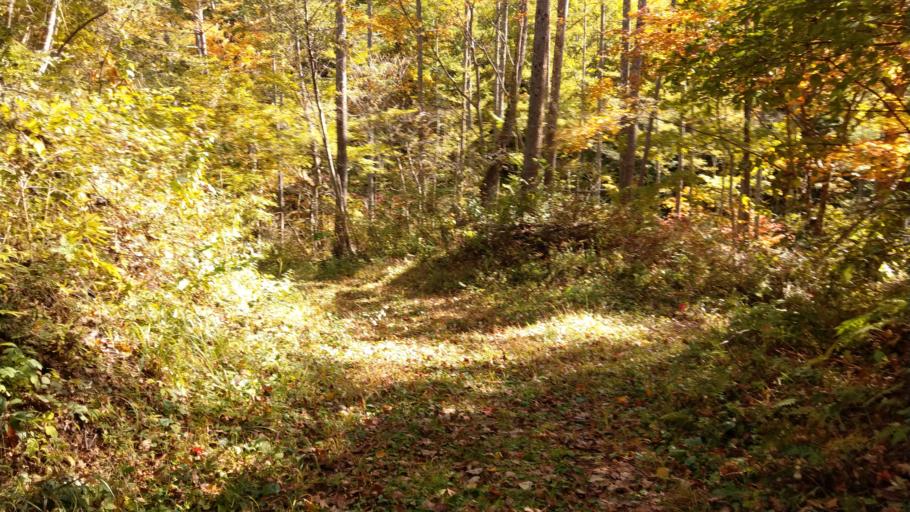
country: JP
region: Nagano
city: Komoro
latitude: 36.3853
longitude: 138.4375
